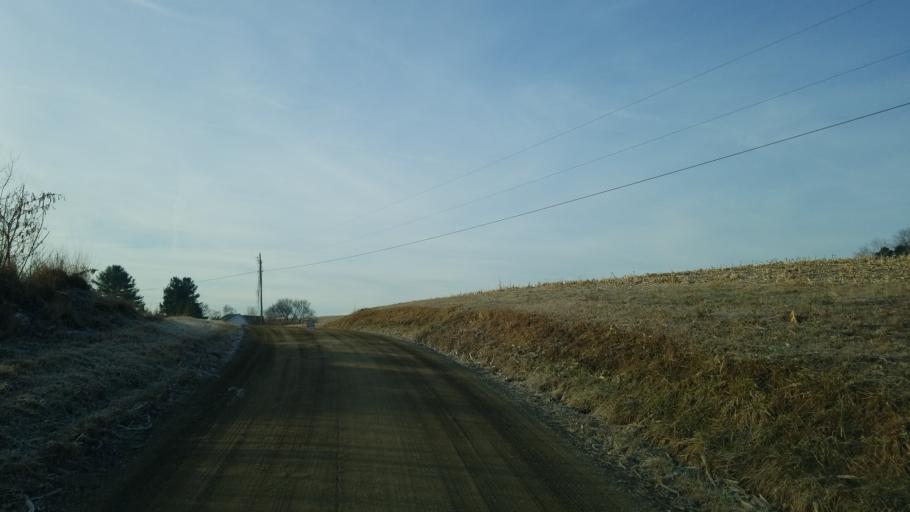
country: US
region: Pennsylvania
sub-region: Indiana County
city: Chevy Chase Heights
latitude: 40.8523
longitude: -79.2481
